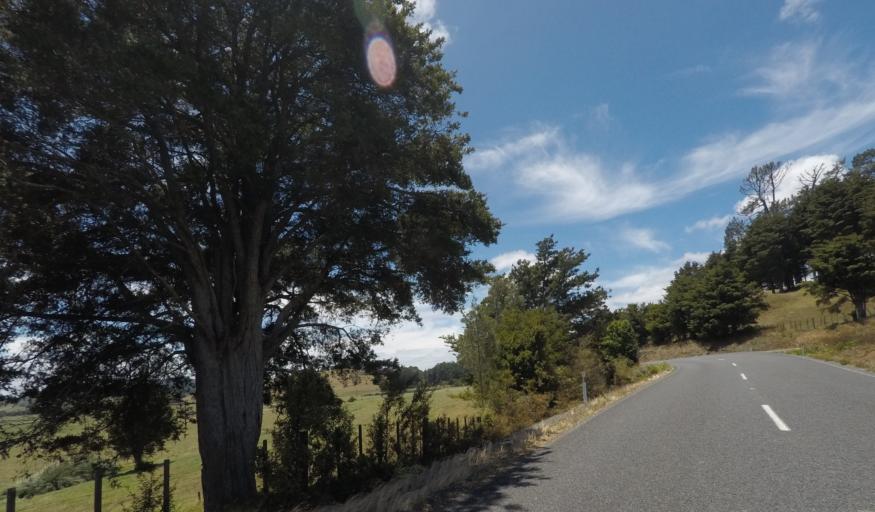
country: NZ
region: Northland
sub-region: Whangarei
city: Whangarei
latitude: -35.5494
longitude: 174.2995
